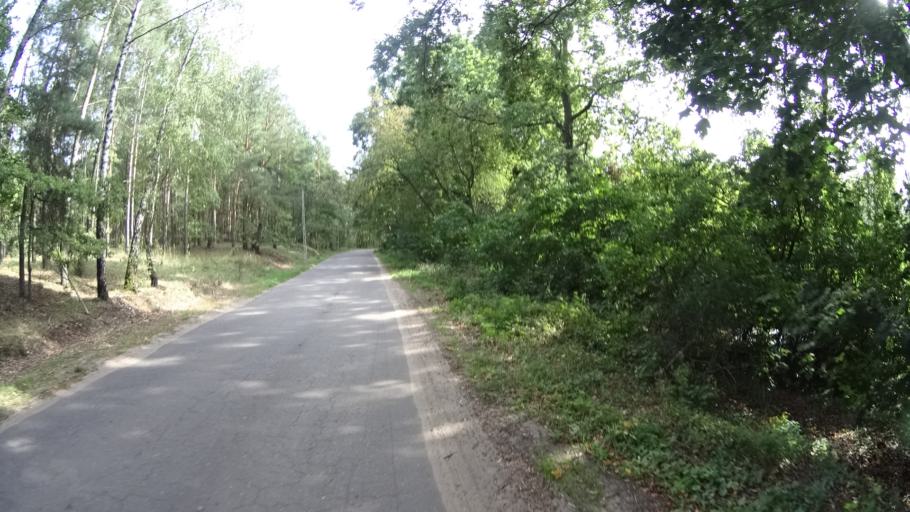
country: PL
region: Masovian Voivodeship
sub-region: Powiat legionowski
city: Serock
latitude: 52.4953
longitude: 21.0844
